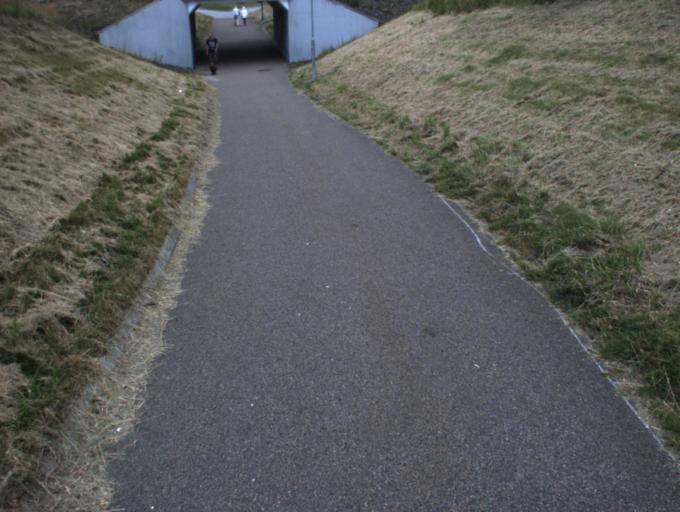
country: SE
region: Skane
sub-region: Helsingborg
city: Rydeback
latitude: 55.9647
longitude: 12.7787
